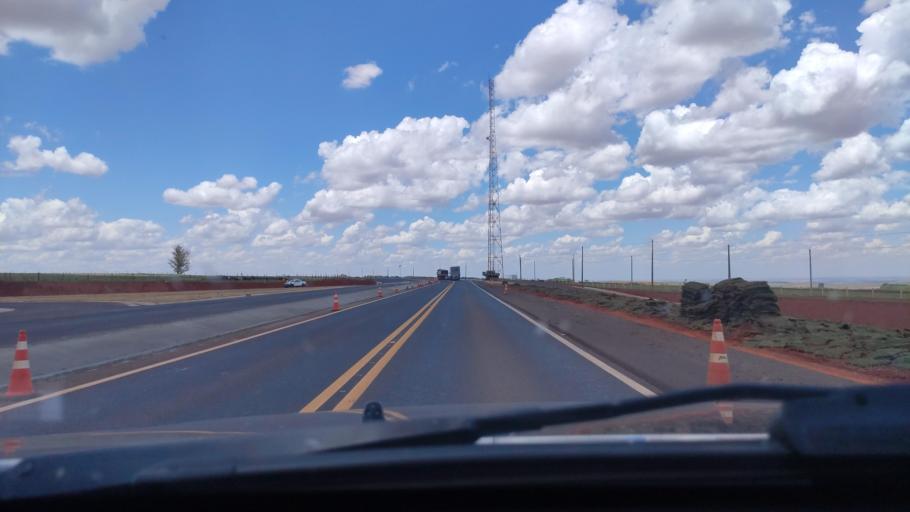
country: BR
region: Sao Paulo
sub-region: Jau
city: Jau
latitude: -22.1857
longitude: -48.4991
